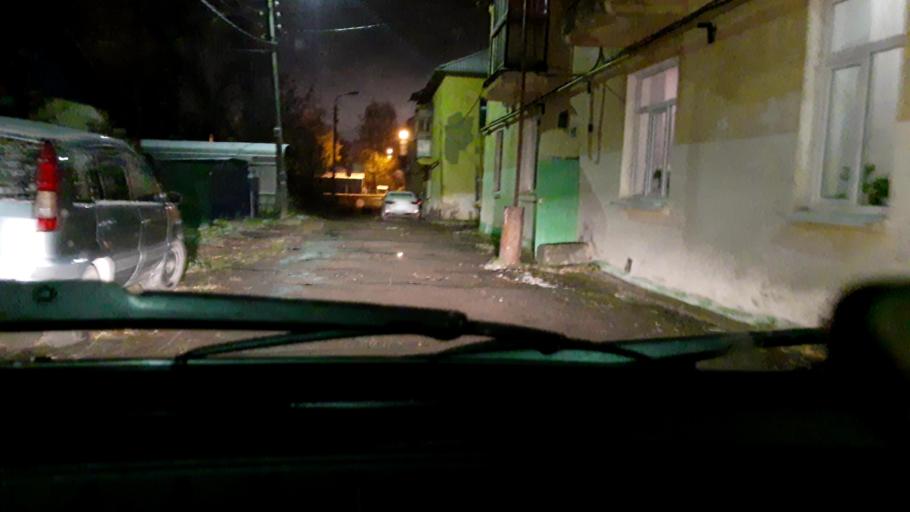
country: RU
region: Bashkortostan
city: Mikhaylovka
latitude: 54.7086
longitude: 55.8295
